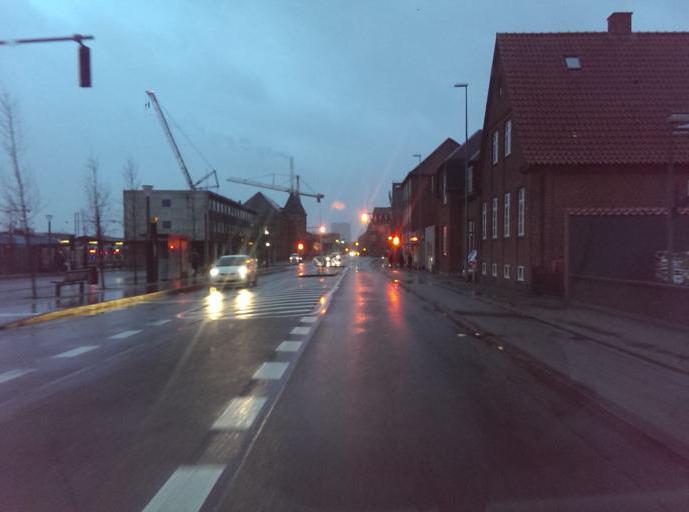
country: DK
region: South Denmark
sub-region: Esbjerg Kommune
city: Esbjerg
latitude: 55.4695
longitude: 8.4585
